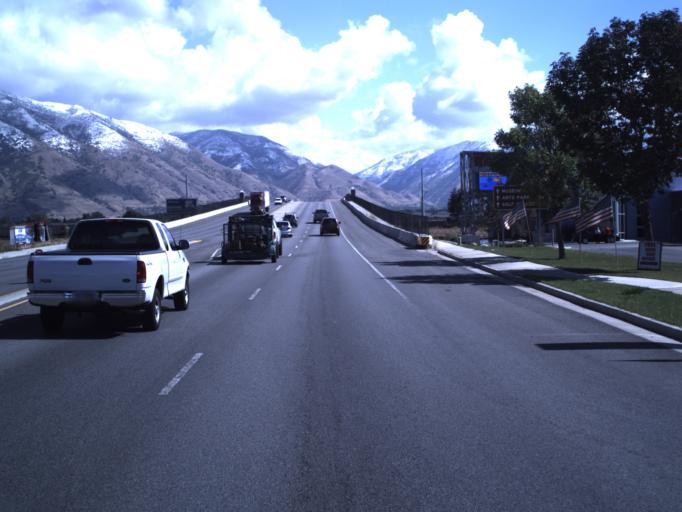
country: US
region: Utah
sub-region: Utah County
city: Springville
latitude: 40.1612
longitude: -111.6415
